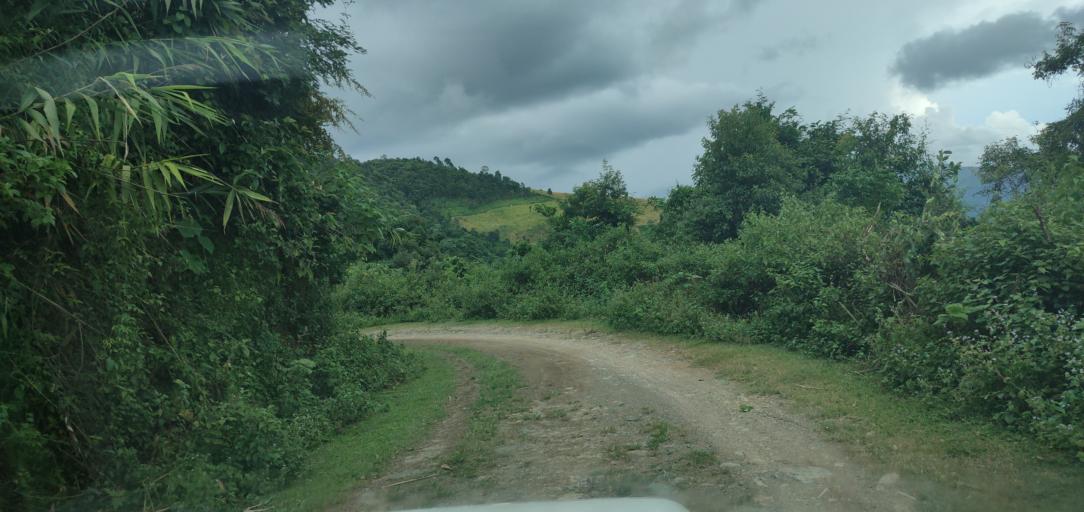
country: LA
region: Phongsali
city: Phongsali
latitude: 21.4469
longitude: 102.3099
